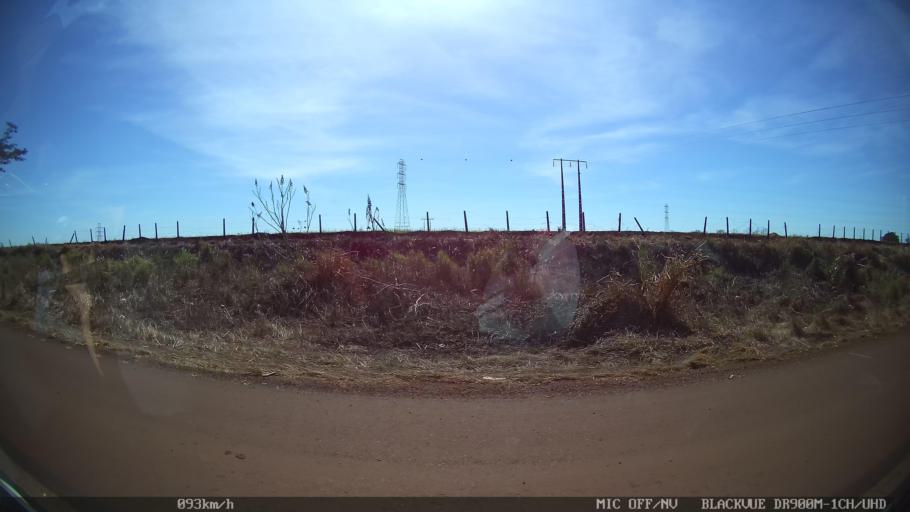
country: BR
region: Sao Paulo
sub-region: Sao Joaquim Da Barra
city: Sao Joaquim da Barra
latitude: -20.5225
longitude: -47.8512
